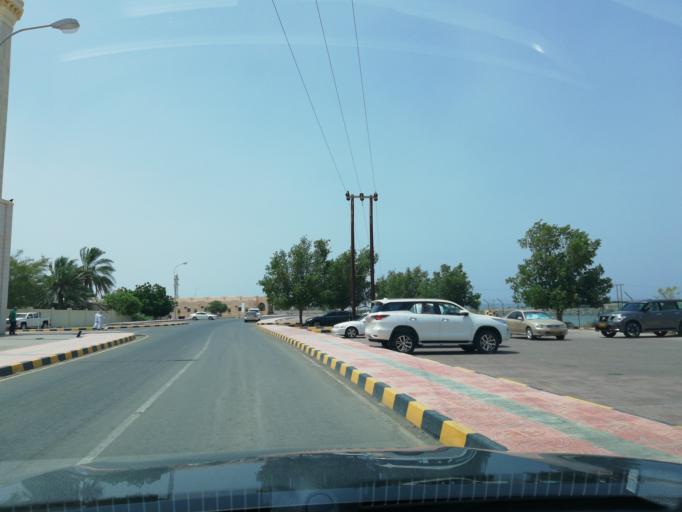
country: OM
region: Al Batinah
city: Shinas
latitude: 24.7432
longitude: 56.4685
